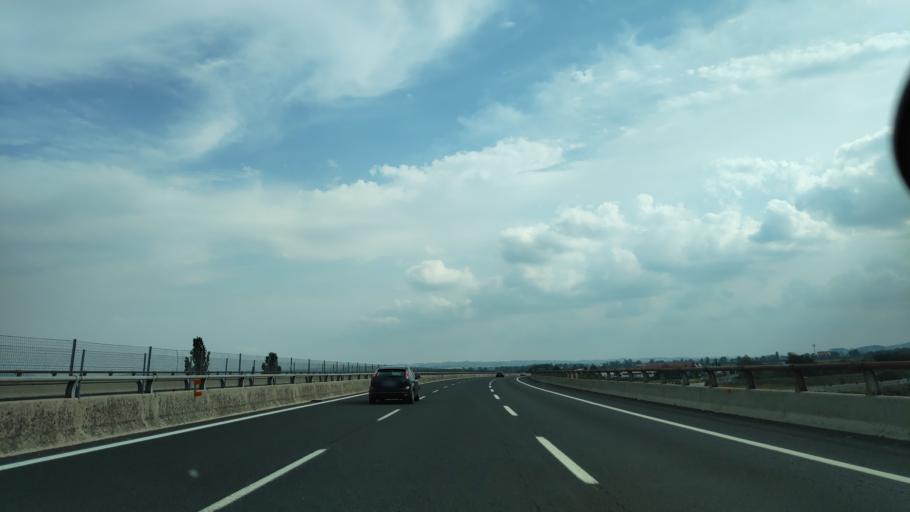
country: IT
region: Latium
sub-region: Citta metropolitana di Roma Capitale
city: Fiano Romano
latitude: 42.1510
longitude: 12.6245
